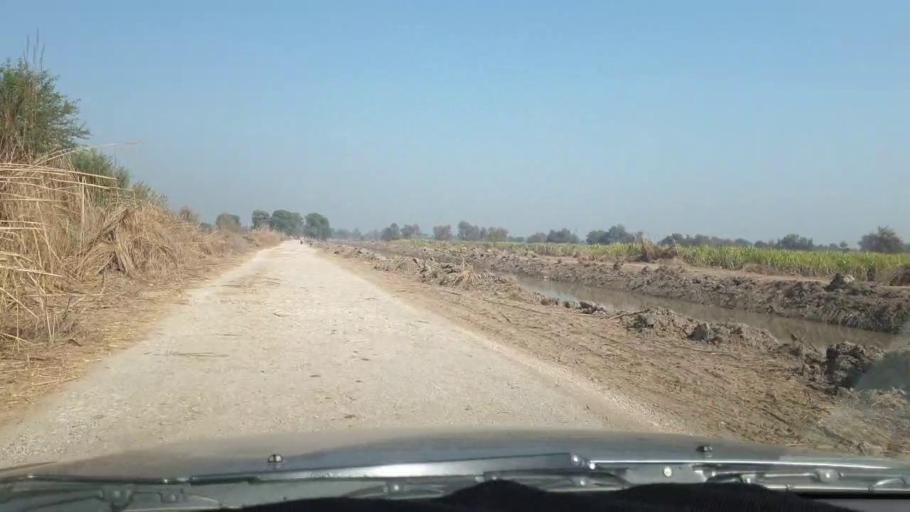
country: PK
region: Sindh
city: Khanpur
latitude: 27.7706
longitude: 69.5338
